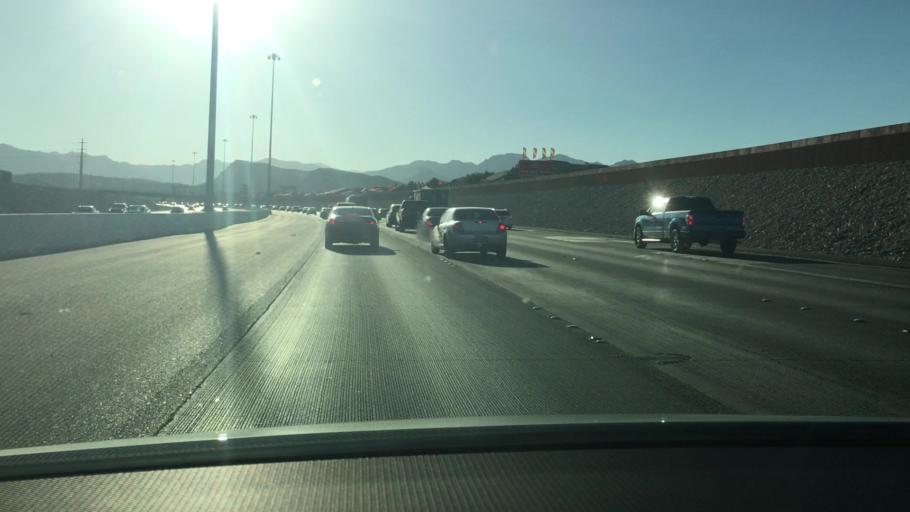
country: US
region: Nevada
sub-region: Clark County
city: Summerlin South
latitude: 36.1173
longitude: -115.3066
